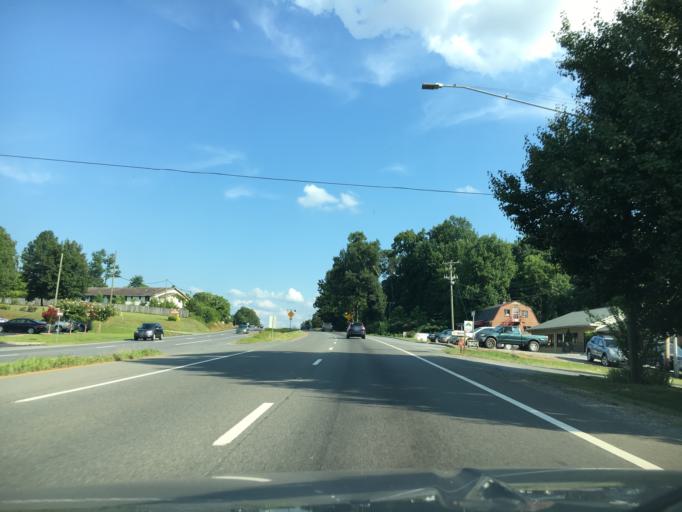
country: US
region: Virginia
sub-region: Franklin County
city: Rocky Mount
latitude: 37.0494
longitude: -79.8814
